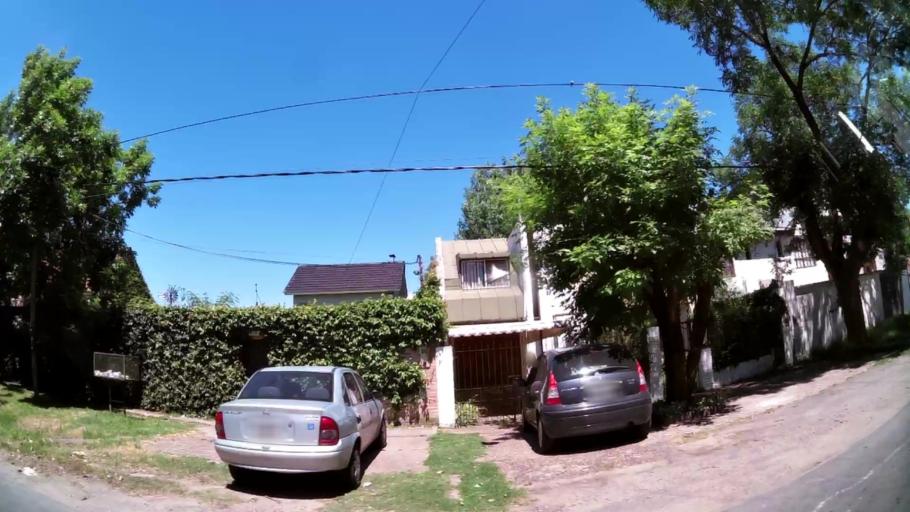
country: AR
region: Buenos Aires
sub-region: Partido de Tigre
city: Tigre
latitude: -34.4948
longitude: -58.6417
